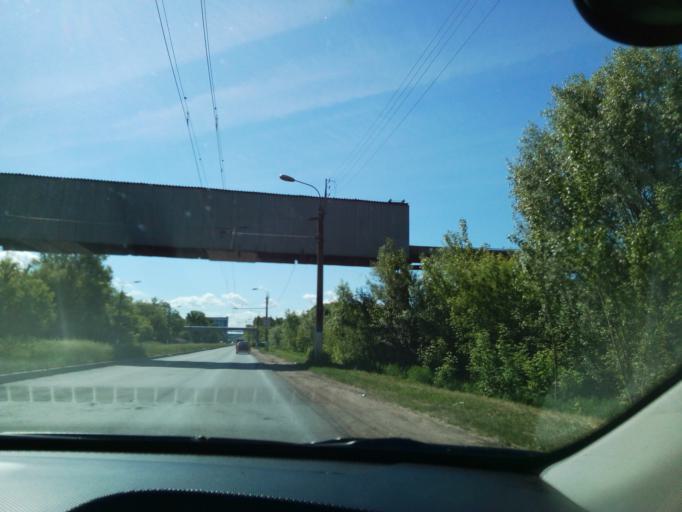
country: RU
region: Chuvashia
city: Novocheboksarsk
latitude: 56.0832
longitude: 47.5043
